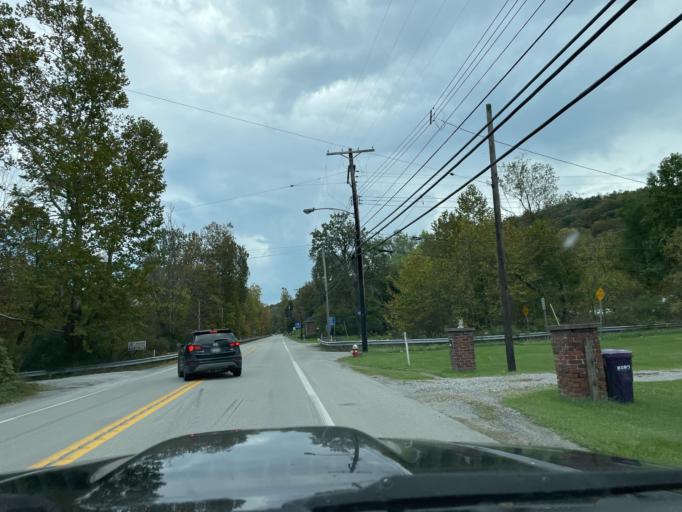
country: US
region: Pennsylvania
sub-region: Westmoreland County
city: Lower Burrell
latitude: 40.5375
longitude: -79.7195
